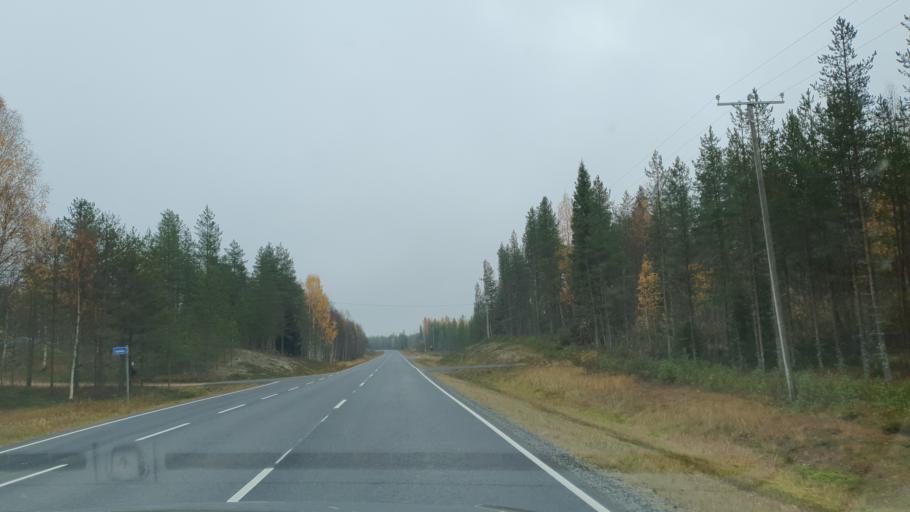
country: FI
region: Lapland
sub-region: Rovaniemi
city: Ranua
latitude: 66.1388
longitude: 26.2730
